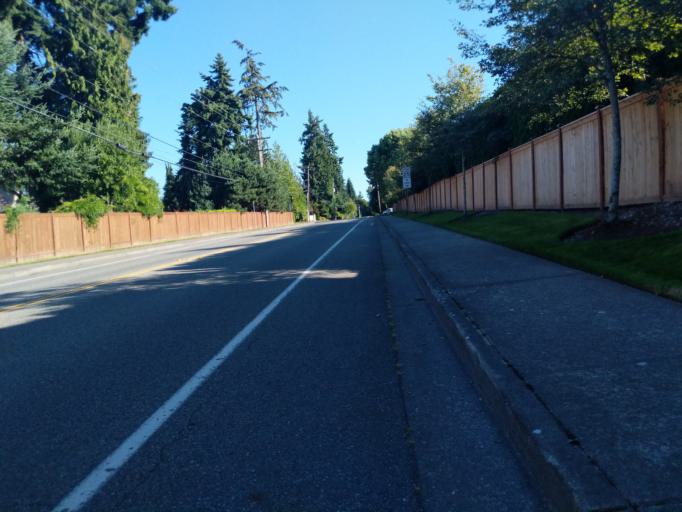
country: US
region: Washington
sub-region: King County
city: Bothell
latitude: 47.7811
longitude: -122.2021
